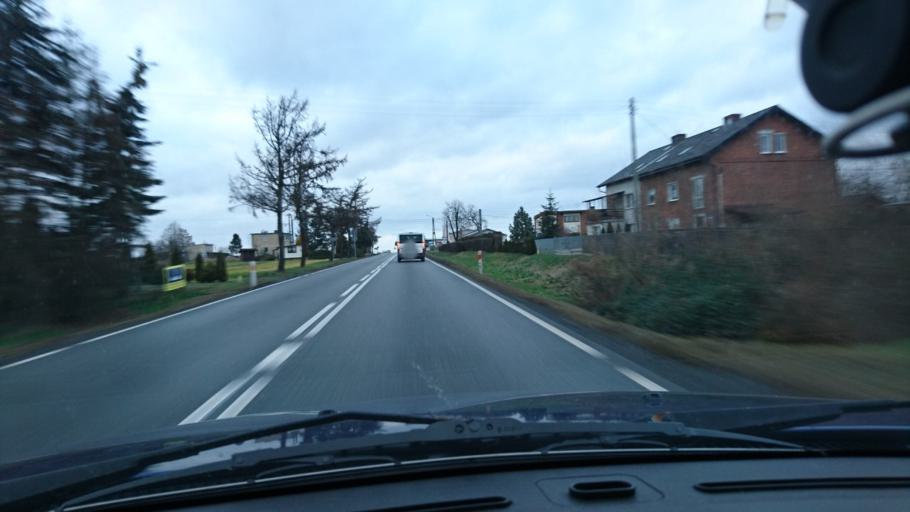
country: PL
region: Opole Voivodeship
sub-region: Powiat kluczborski
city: Kluczbork
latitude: 51.0070
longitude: 18.2046
